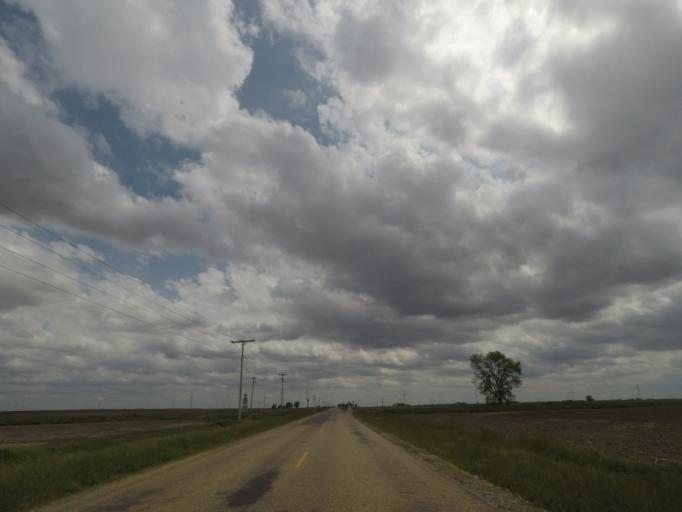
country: US
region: Illinois
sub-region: Macon County
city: Maroa
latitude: 40.0724
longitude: -89.0860
